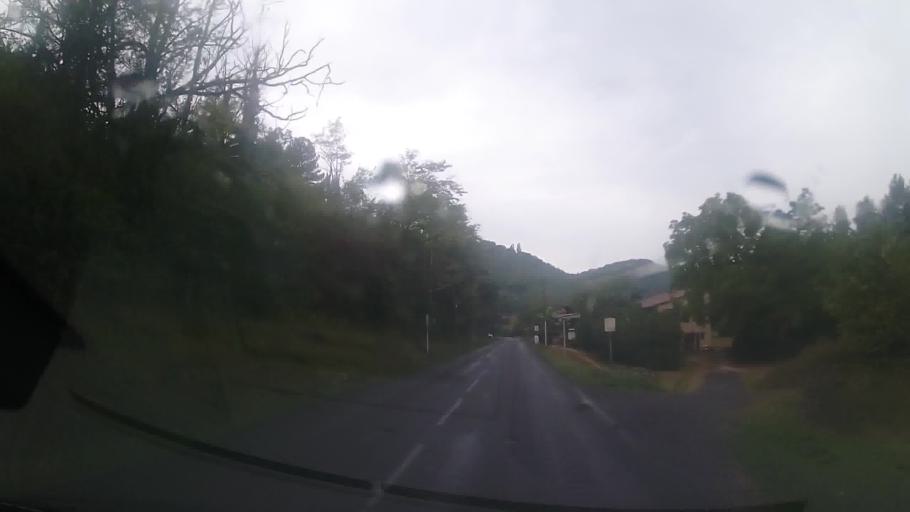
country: FR
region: Aquitaine
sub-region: Departement de la Dordogne
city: Cenac-et-Saint-Julien
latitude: 44.7887
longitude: 1.1649
